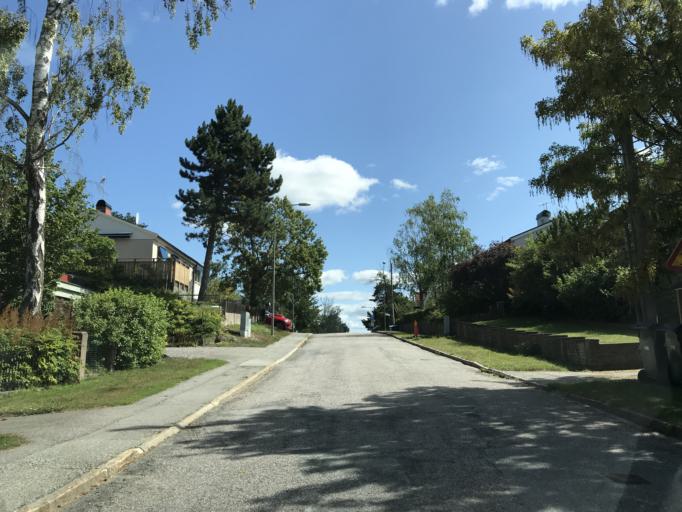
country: SE
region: Stockholm
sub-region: Huddinge Kommun
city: Segeltorp
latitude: 59.2957
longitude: 17.9497
